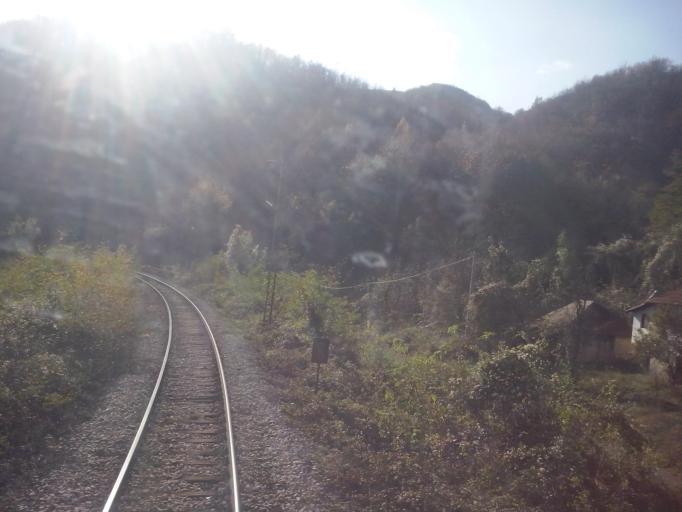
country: RS
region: Central Serbia
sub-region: Kolubarski Okrug
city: Valjevo
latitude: 44.1724
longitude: 19.8679
